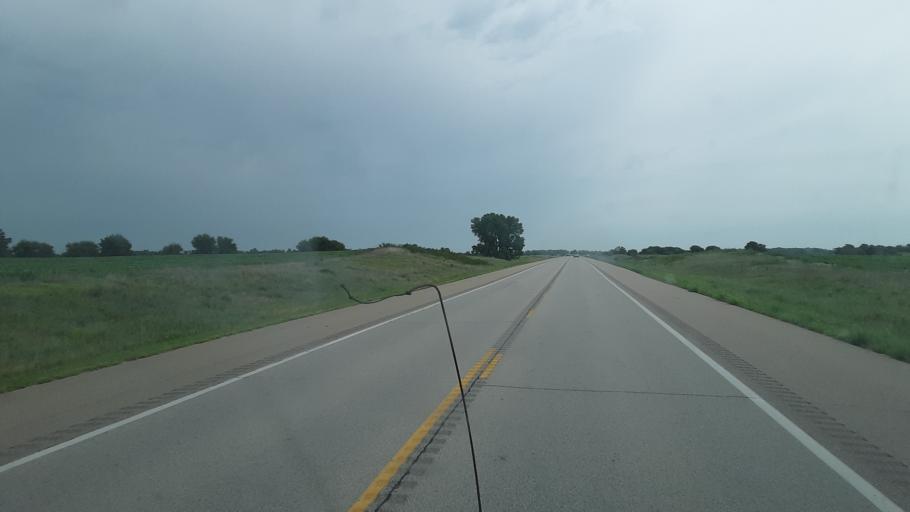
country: US
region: Kansas
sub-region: Stafford County
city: Stafford
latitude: 37.9761
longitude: -98.3972
